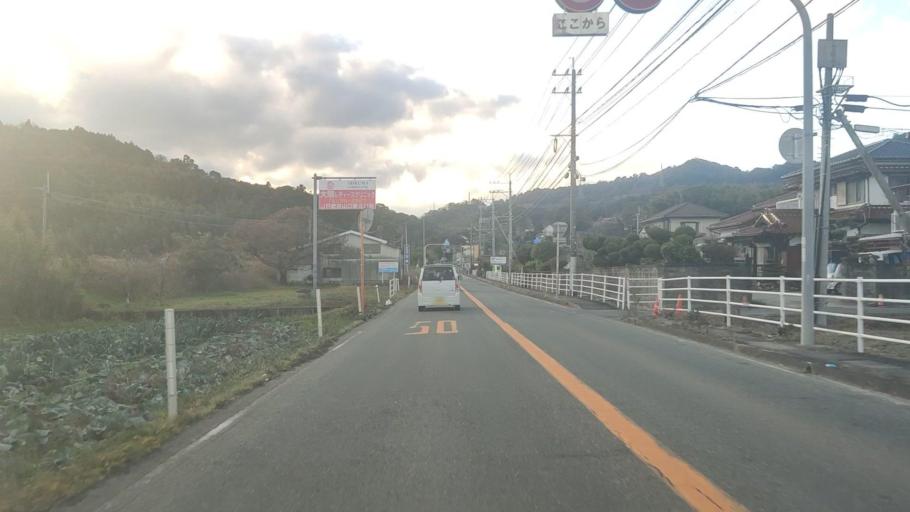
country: JP
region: Saga Prefecture
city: Saga-shi
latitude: 33.2910
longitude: 130.1745
